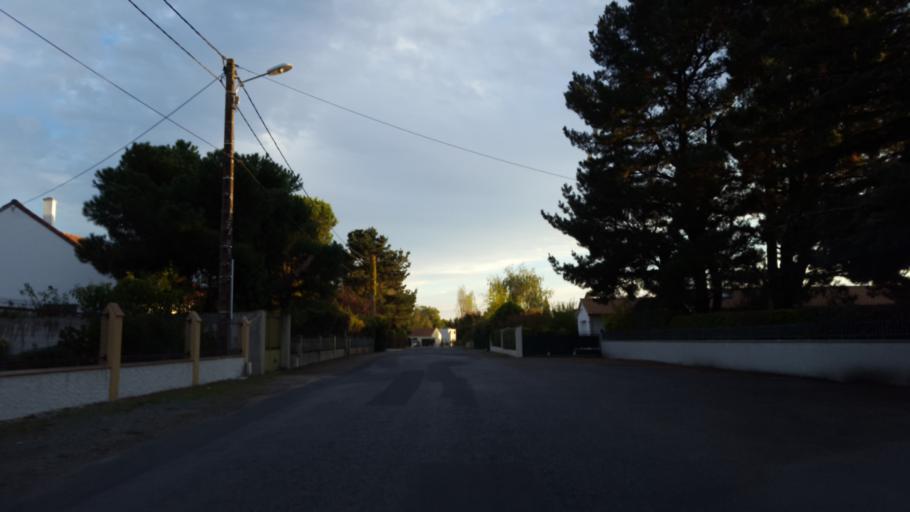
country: FR
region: Pays de la Loire
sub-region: Departement de la Loire-Atlantique
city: Basse-Goulaine
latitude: 47.2099
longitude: -1.4752
